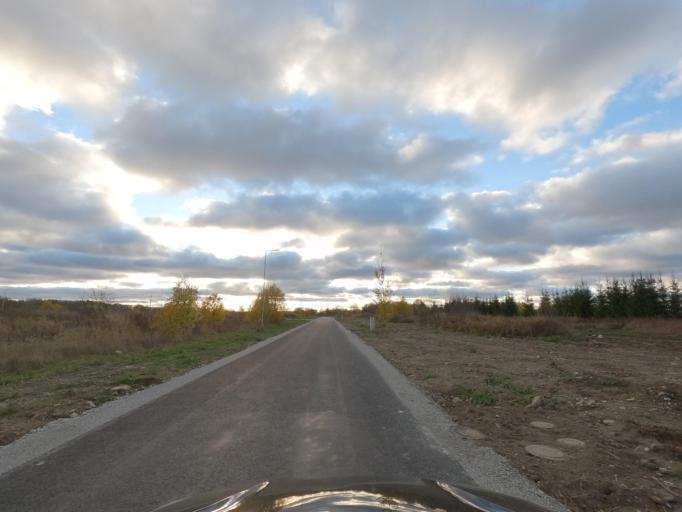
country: EE
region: Harju
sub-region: Rae vald
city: Jueri
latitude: 59.3712
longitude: 24.8448
